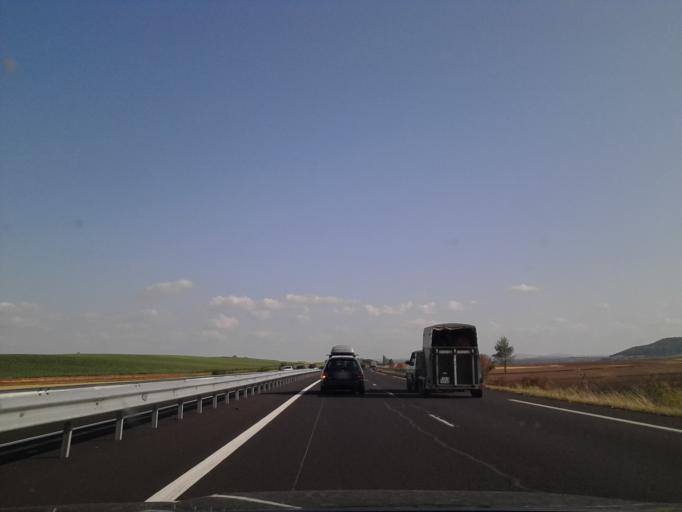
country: FR
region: Auvergne
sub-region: Departement du Puy-de-Dome
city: Le Breuil-sur-Couze
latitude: 45.4403
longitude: 3.2716
